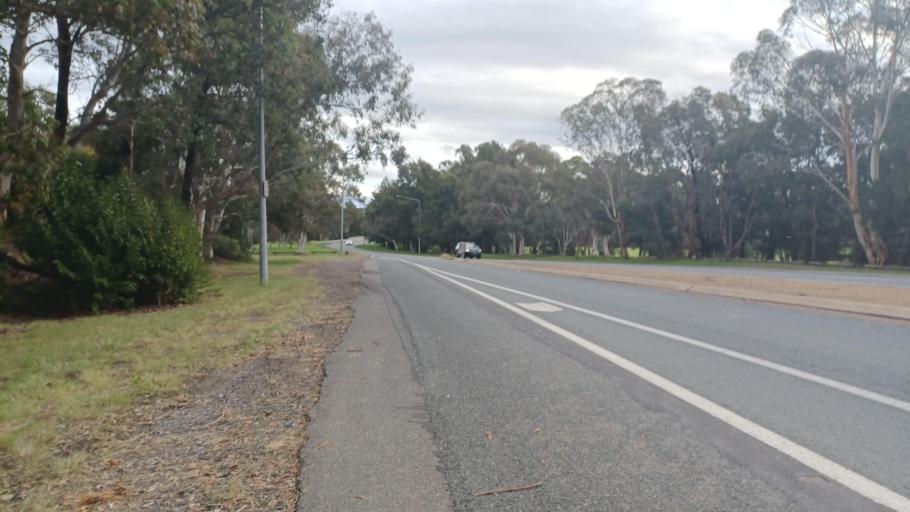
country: AU
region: Australian Capital Territory
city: Belconnen
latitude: -35.2143
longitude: 149.0583
